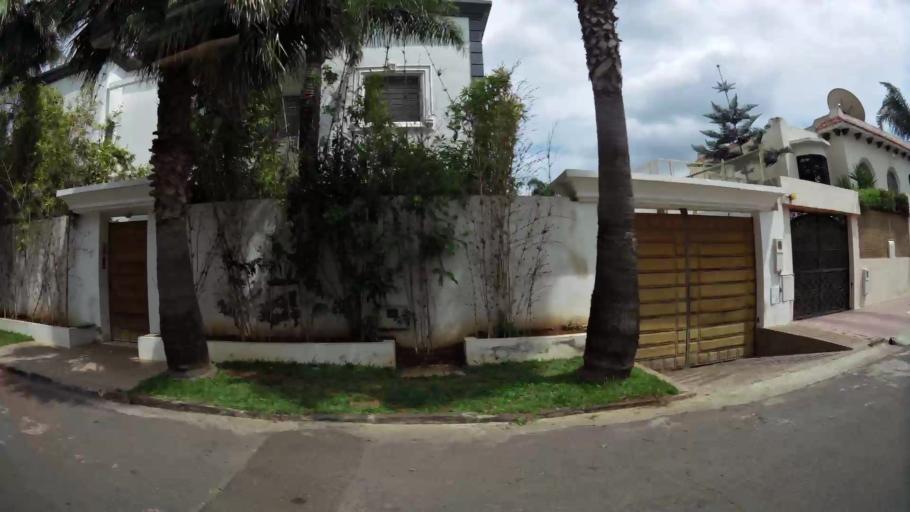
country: MA
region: Grand Casablanca
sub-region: Casablanca
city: Casablanca
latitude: 33.5572
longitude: -7.6430
